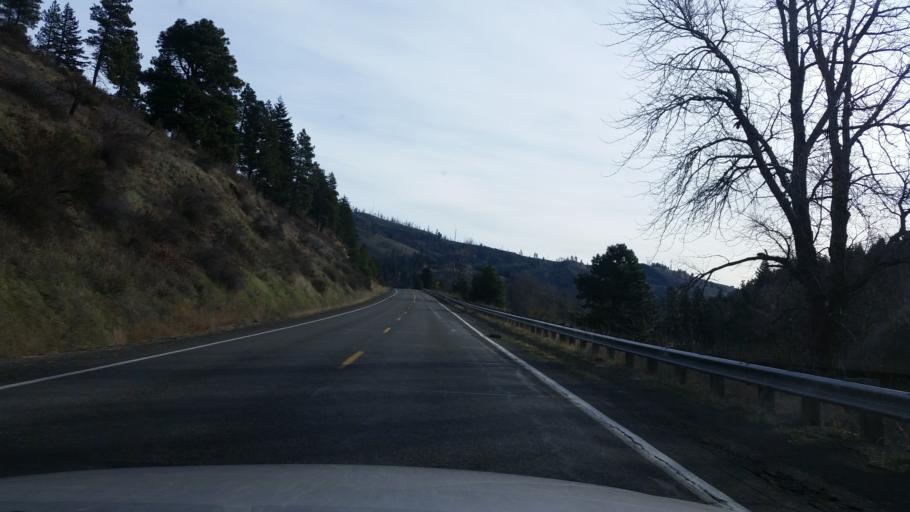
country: US
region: Washington
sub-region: Kittitas County
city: Cle Elum
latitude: 47.1668
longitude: -120.8277
